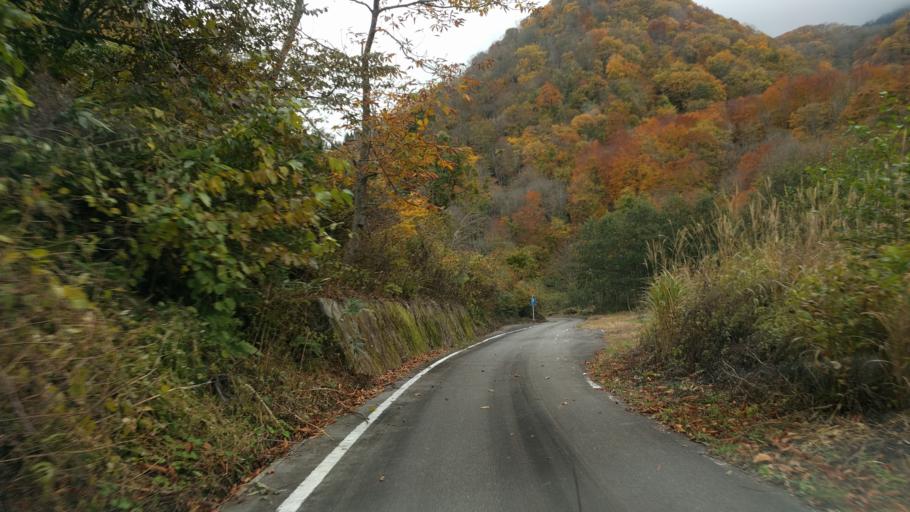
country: JP
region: Fukushima
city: Kitakata
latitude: 37.3890
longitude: 139.7178
